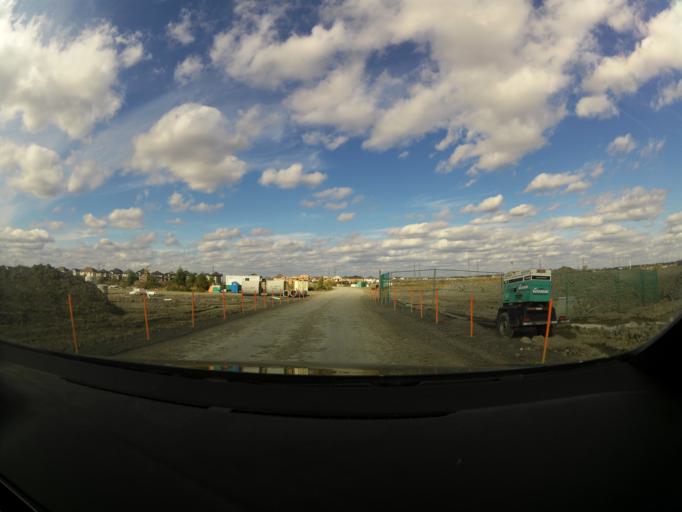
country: CA
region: Ontario
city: Bells Corners
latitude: 45.2718
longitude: -75.8818
